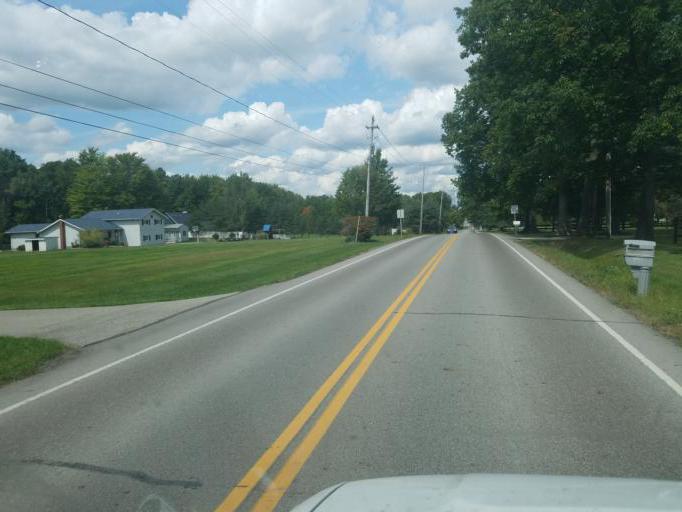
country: US
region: Ohio
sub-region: Geauga County
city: Middlefield
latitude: 41.4188
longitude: -81.0390
